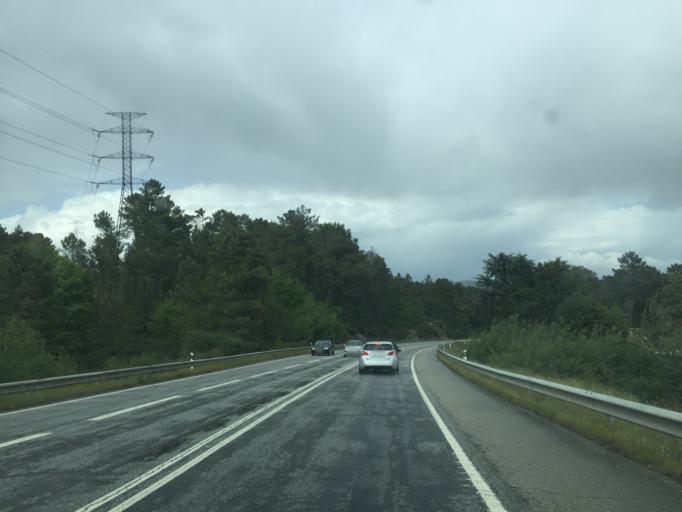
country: PT
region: Viseu
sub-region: Viseu
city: Abraveses
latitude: 40.6587
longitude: -8.0149
